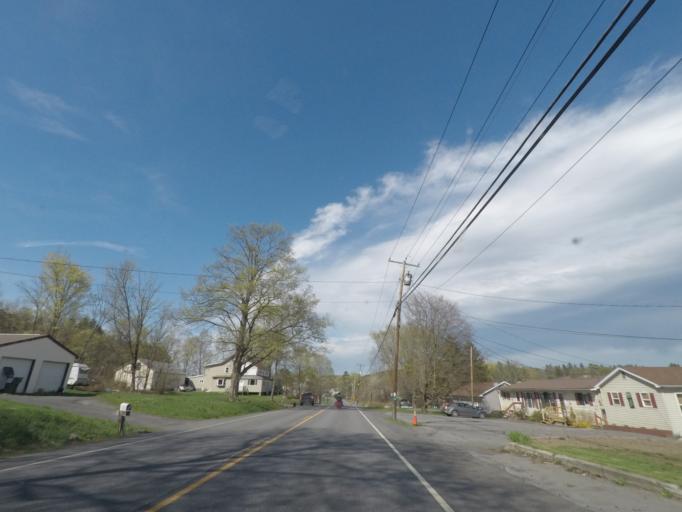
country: US
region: New York
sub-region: Greene County
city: Cairo
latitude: 42.4097
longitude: -74.0236
